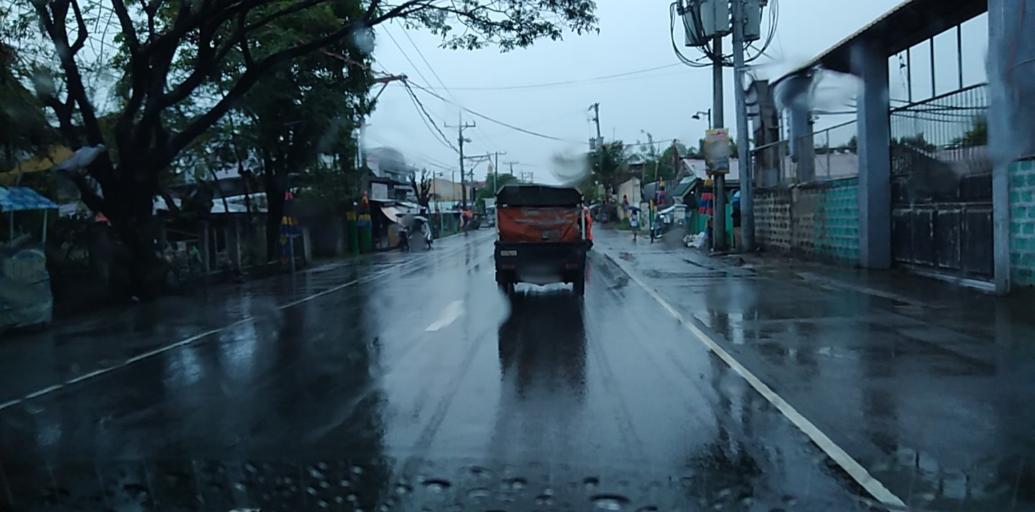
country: PH
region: Central Luzon
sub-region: Province of Bulacan
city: Bulualto
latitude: 15.2093
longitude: 120.9560
